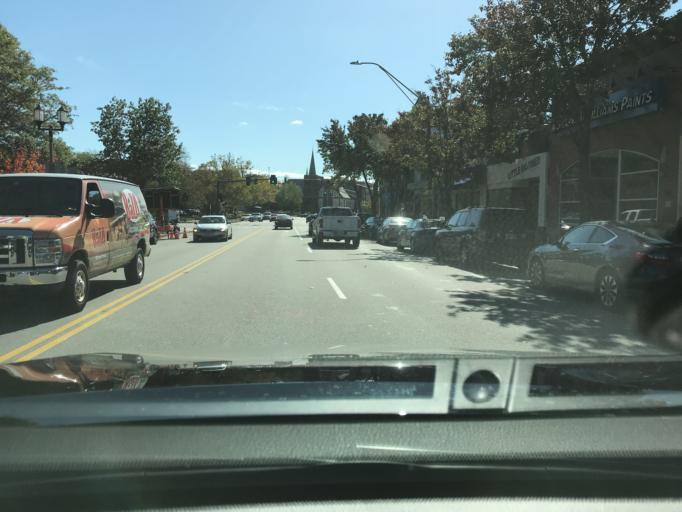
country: US
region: Massachusetts
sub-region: Middlesex County
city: Newton
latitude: 42.3308
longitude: -71.1947
